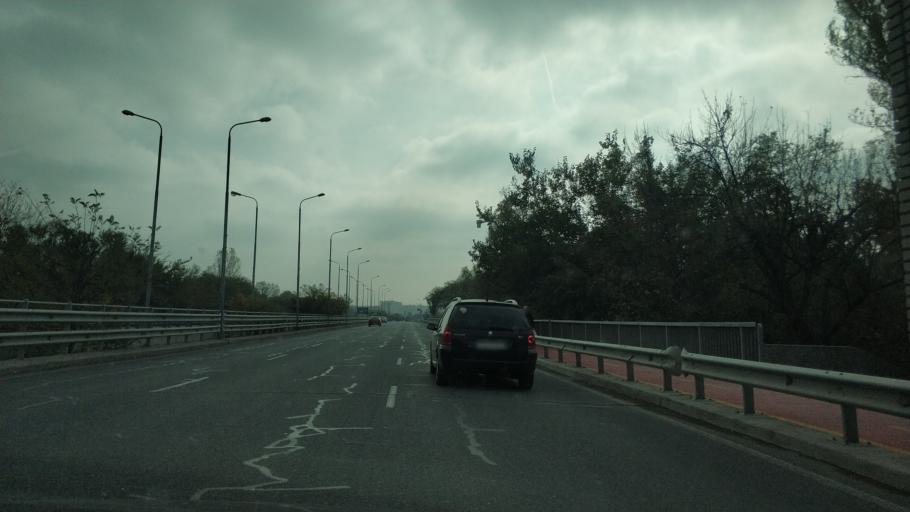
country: BG
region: Plovdiv
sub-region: Obshtina Plovdiv
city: Plovdiv
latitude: 42.1562
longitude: 24.7653
